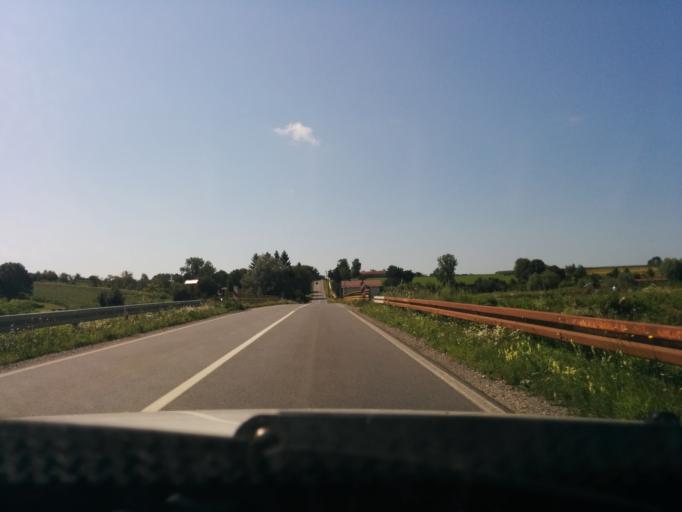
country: HR
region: Sisacko-Moslavacka
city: Lipovljani
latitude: 45.4298
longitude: 16.9045
